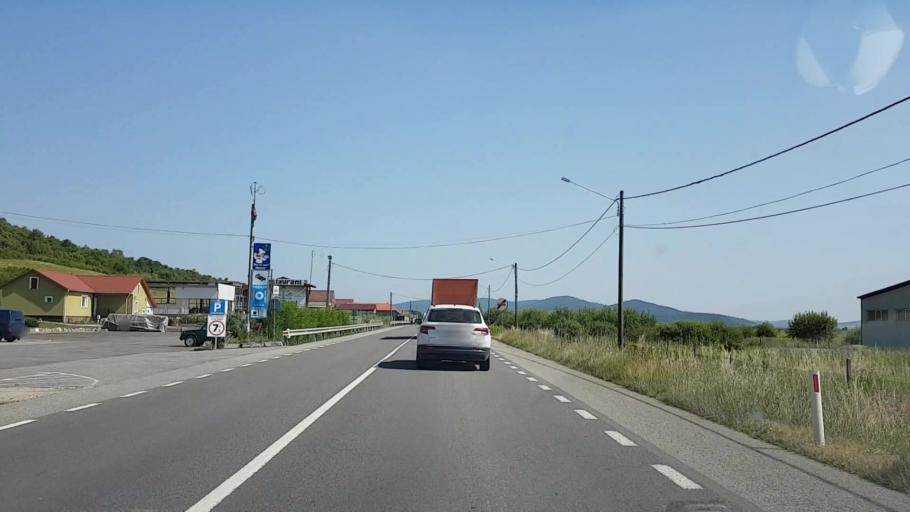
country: RO
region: Bistrita-Nasaud
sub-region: Comuna Sieu-Odorhei
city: Sieu-Odorhei
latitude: 47.1355
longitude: 24.3081
